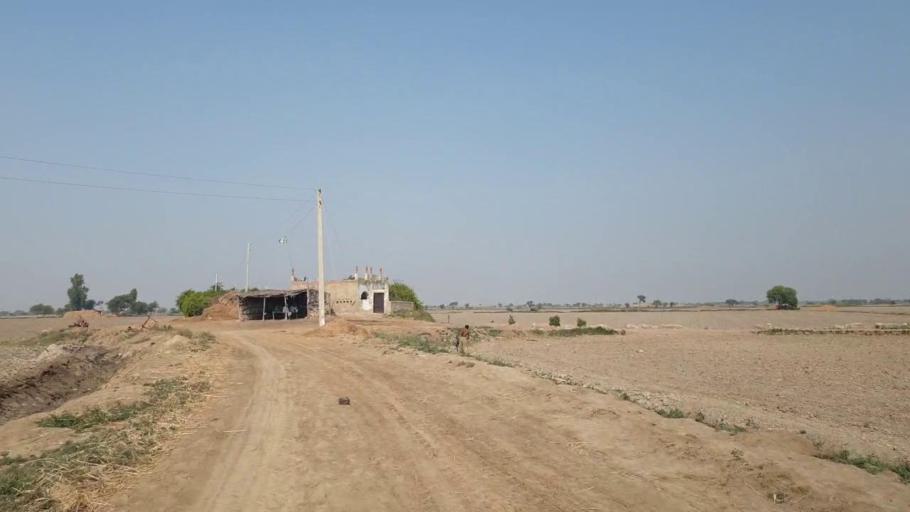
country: PK
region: Sindh
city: Matli
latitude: 24.9803
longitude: 68.5905
